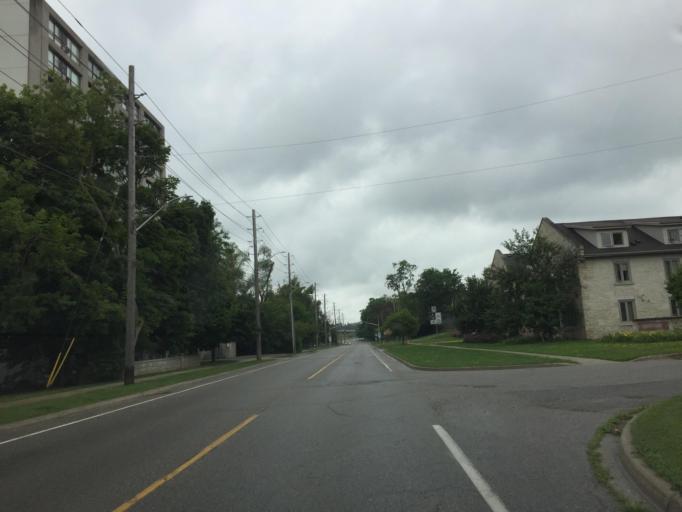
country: CA
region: Ontario
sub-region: Wellington County
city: Guelph
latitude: 43.5322
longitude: -80.2596
